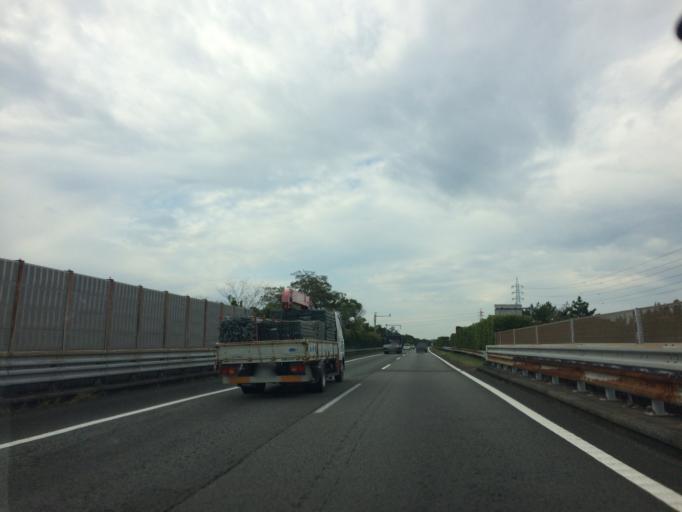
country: JP
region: Shizuoka
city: Fujieda
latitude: 34.8157
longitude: 138.2634
